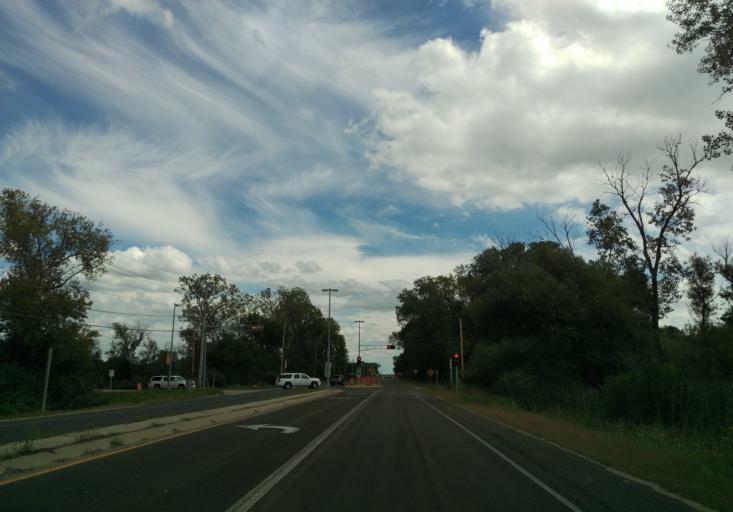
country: US
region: Wisconsin
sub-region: Dane County
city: Waunakee
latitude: 43.1476
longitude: -89.4332
